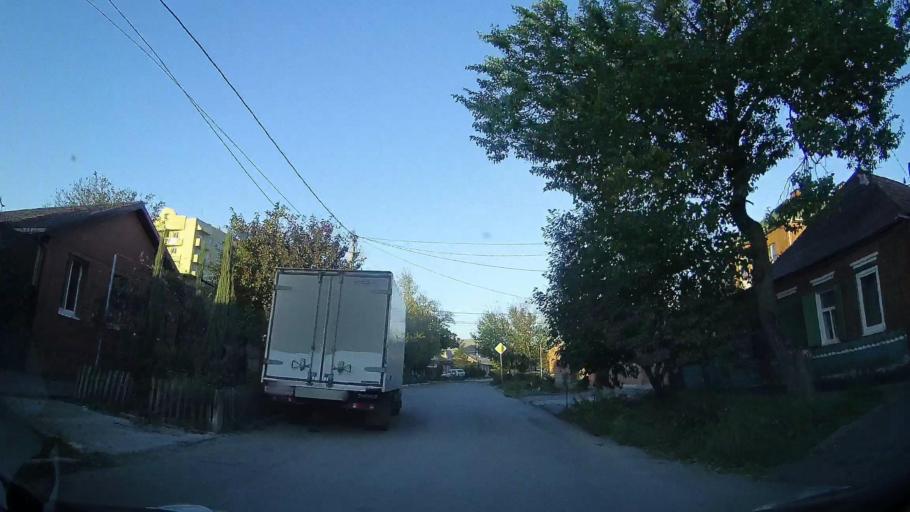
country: RU
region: Rostov
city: Rostov-na-Donu
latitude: 47.2428
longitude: 39.6747
